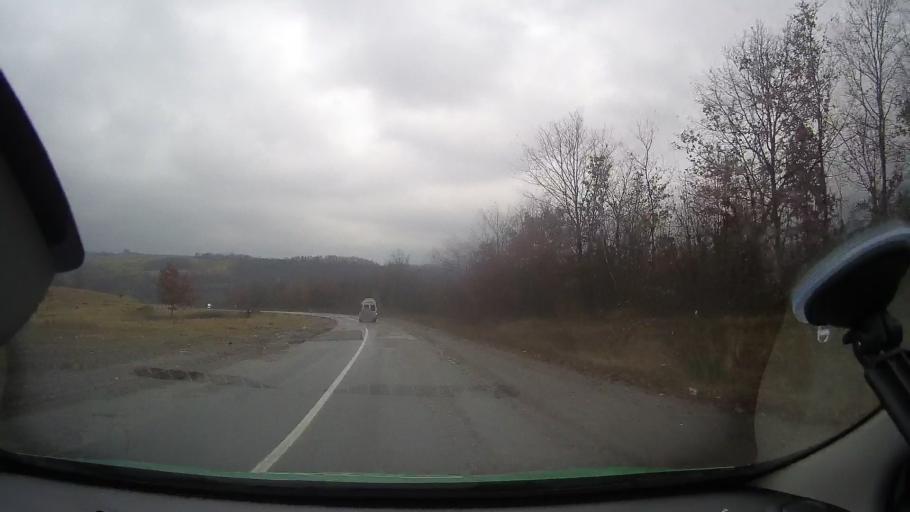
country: RO
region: Arad
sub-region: Comuna Varfurile
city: Varfurile
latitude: 46.2921
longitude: 22.5420
